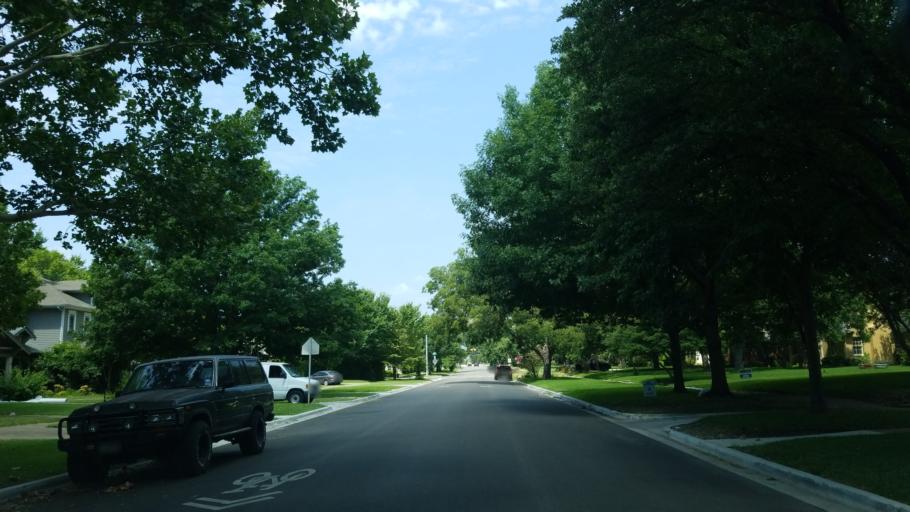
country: US
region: Texas
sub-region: Dallas County
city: Highland Park
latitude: 32.8174
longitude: -96.7666
